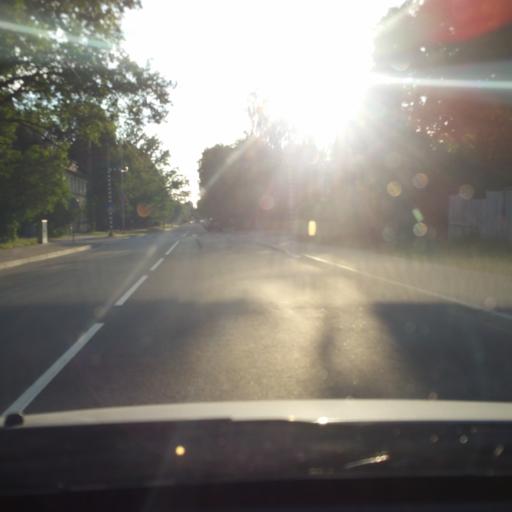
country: LV
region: Riga
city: Jaunciems
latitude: 56.9690
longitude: 24.1885
